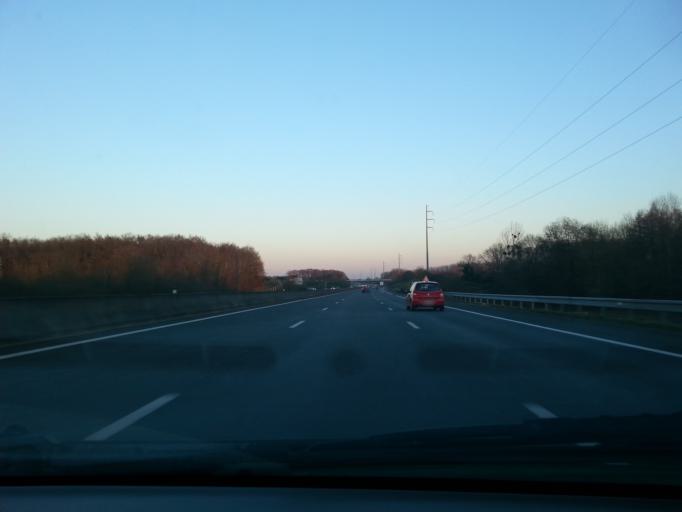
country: FR
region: Centre
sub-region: Departement d'Eure-et-Loir
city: Yevres
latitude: 48.2821
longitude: 1.2312
